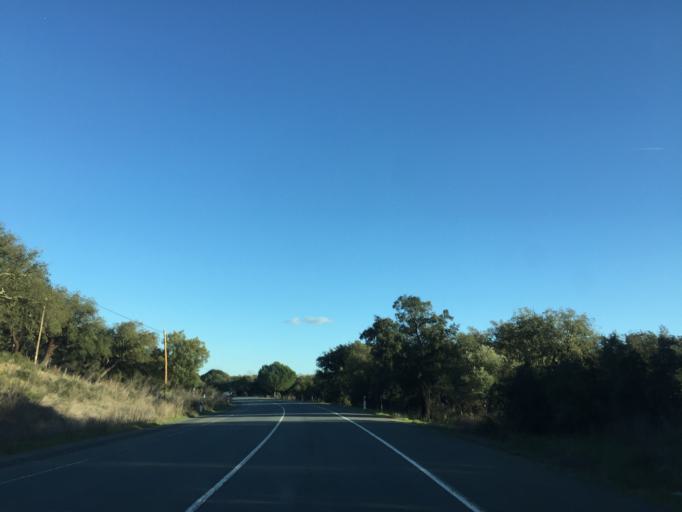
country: PT
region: Setubal
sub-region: Grandola
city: Grandola
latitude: 38.1234
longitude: -8.4540
